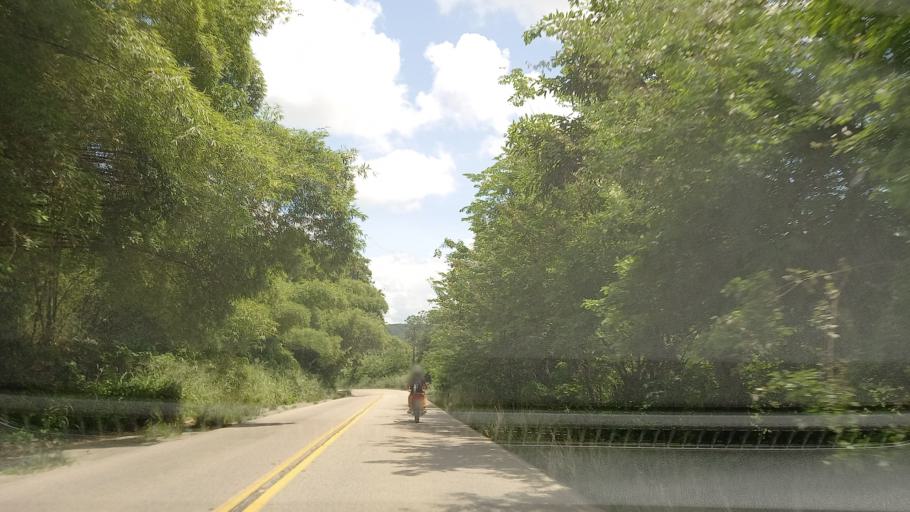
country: BR
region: Pernambuco
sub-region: Rio Formoso
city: Rio Formoso
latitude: -8.6566
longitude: -35.1402
